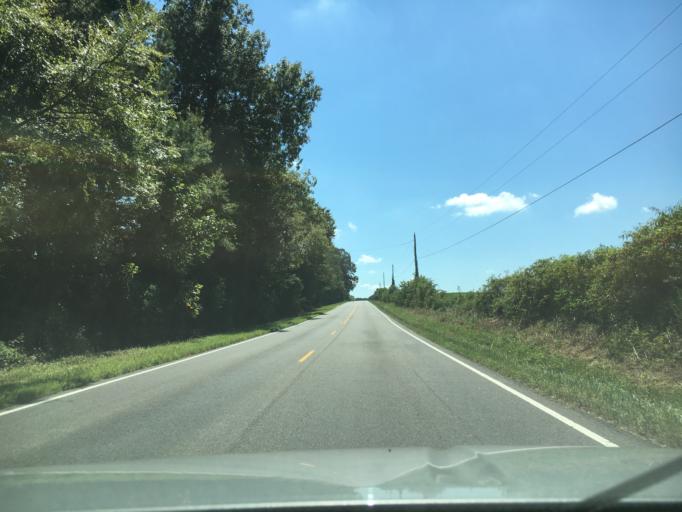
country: US
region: Virginia
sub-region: Amelia County
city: Amelia Court House
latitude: 37.4025
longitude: -77.8965
